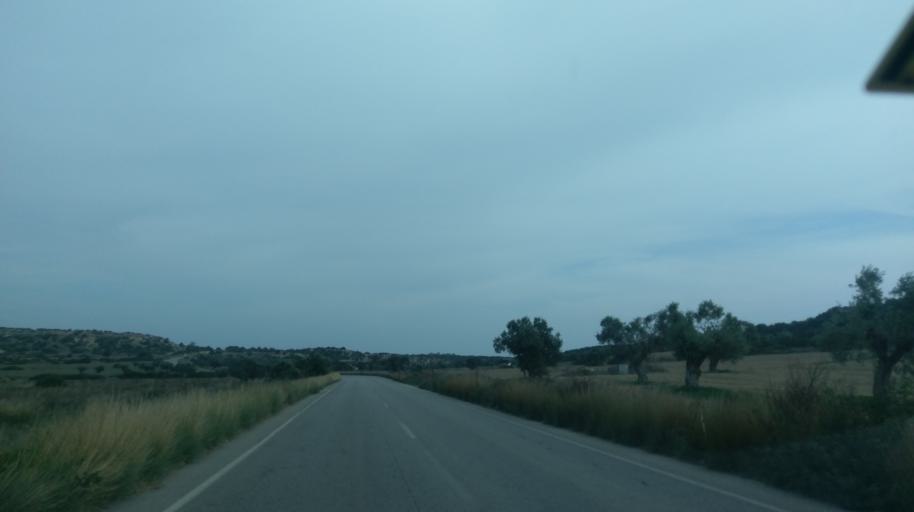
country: CY
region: Ammochostos
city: Leonarisso
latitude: 35.4013
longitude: 34.0927
